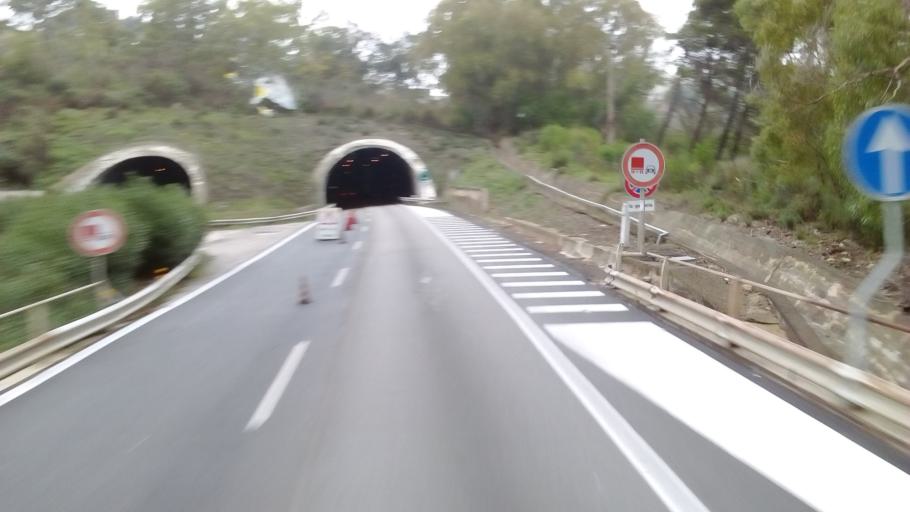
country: IT
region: Sicily
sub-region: Enna
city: Calascibetta
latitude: 37.5797
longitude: 14.2877
